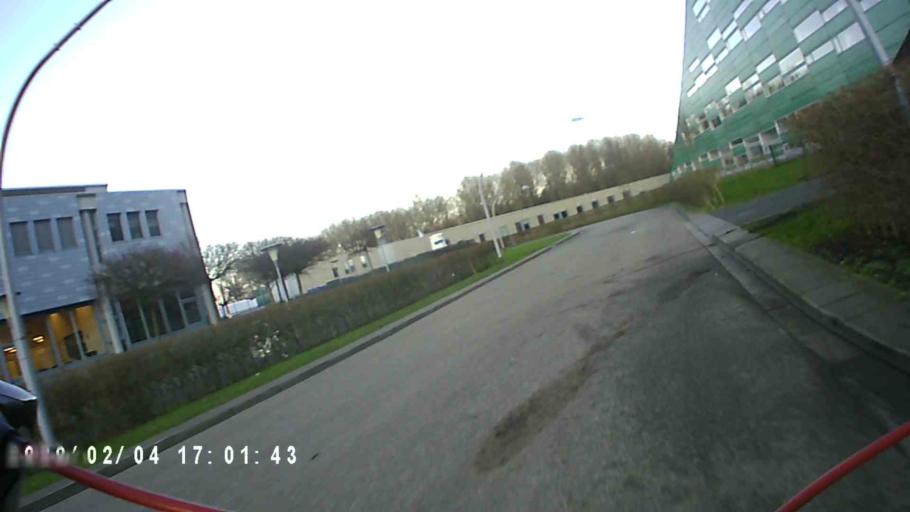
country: NL
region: Groningen
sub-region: Gemeente Groningen
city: Korrewegwijk
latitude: 53.2416
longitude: 6.5373
